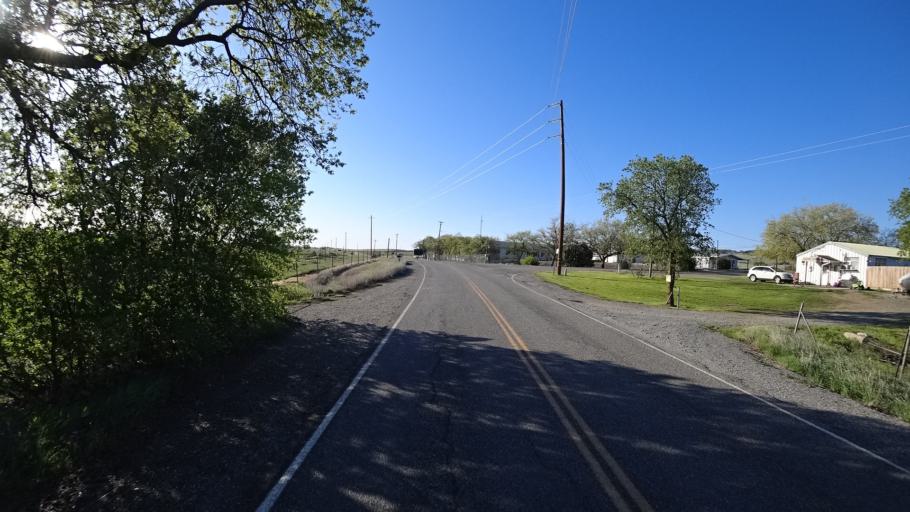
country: US
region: California
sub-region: Glenn County
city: Orland
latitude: 39.8073
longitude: -122.3301
